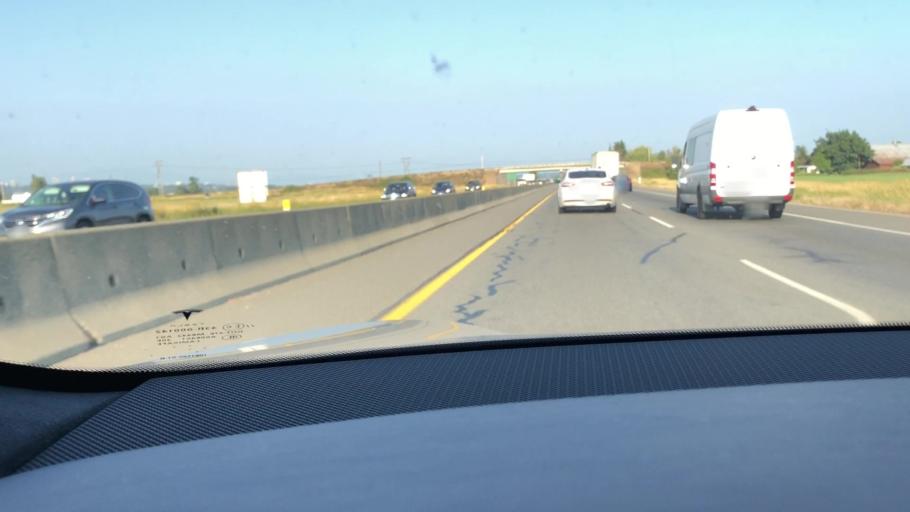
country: CA
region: British Columbia
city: Richmond
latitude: 49.1778
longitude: -123.0517
